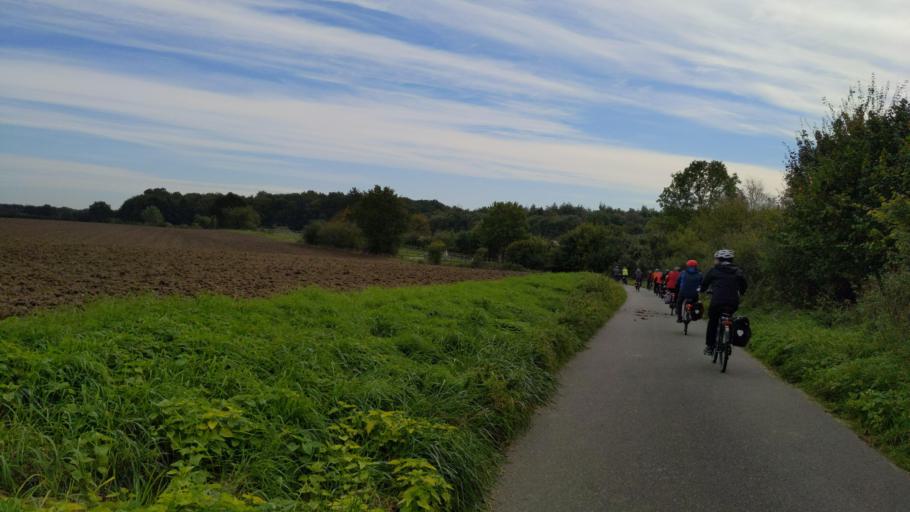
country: DE
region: Schleswig-Holstein
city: Rehhorst
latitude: 53.8693
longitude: 10.4772
